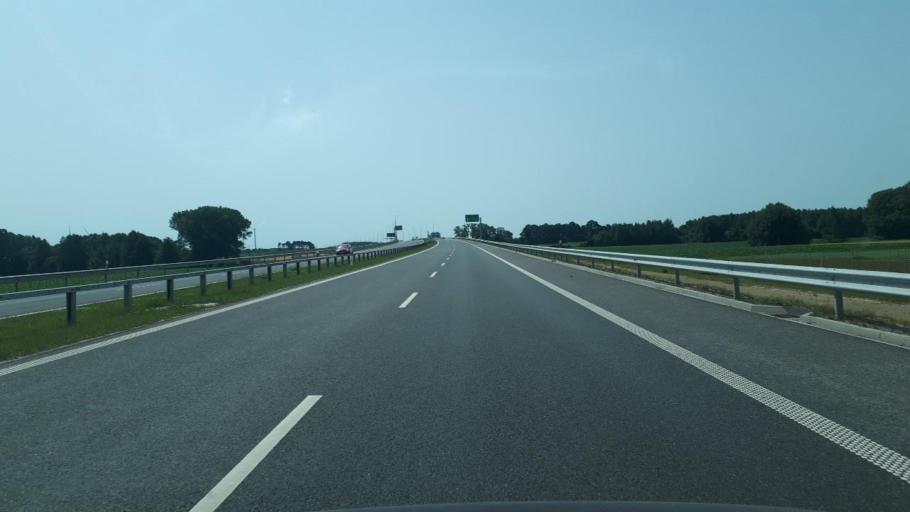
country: PL
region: Greater Poland Voivodeship
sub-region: Powiat kepinski
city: Kepno
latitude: 51.3009
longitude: 18.0181
